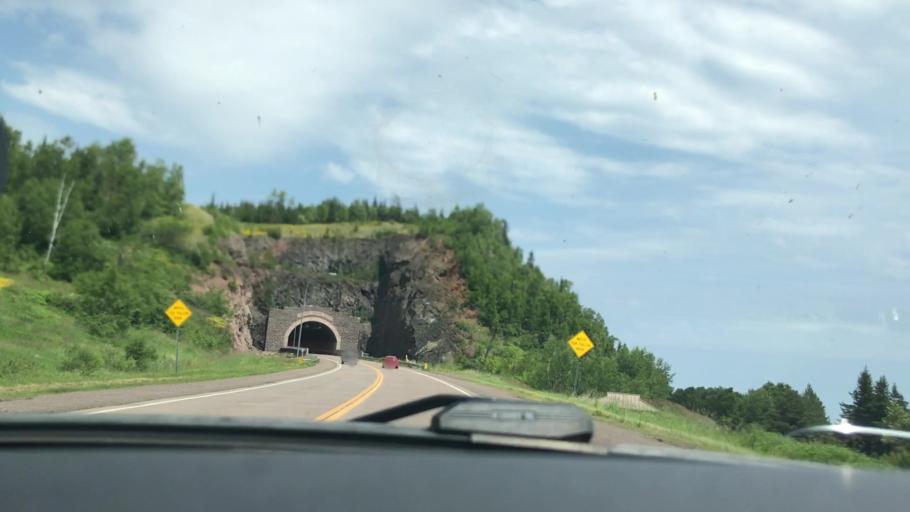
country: US
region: Minnesota
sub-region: Lake County
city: Two Harbors
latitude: 47.0656
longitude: -91.5990
